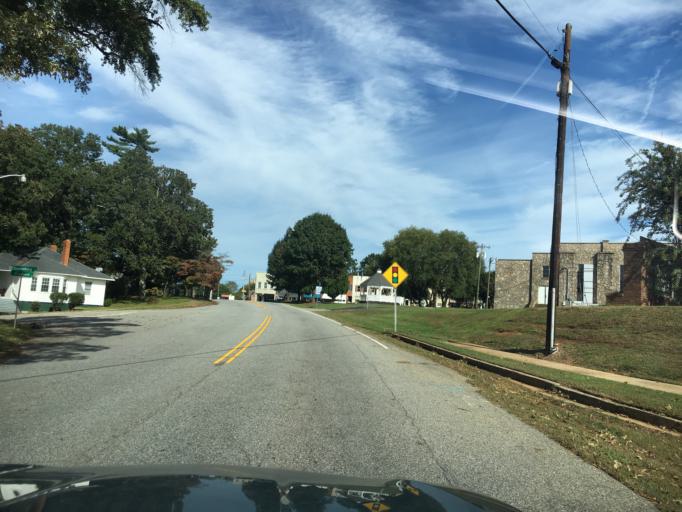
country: US
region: South Carolina
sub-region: Spartanburg County
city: Lyman
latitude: 34.9492
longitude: -82.1250
